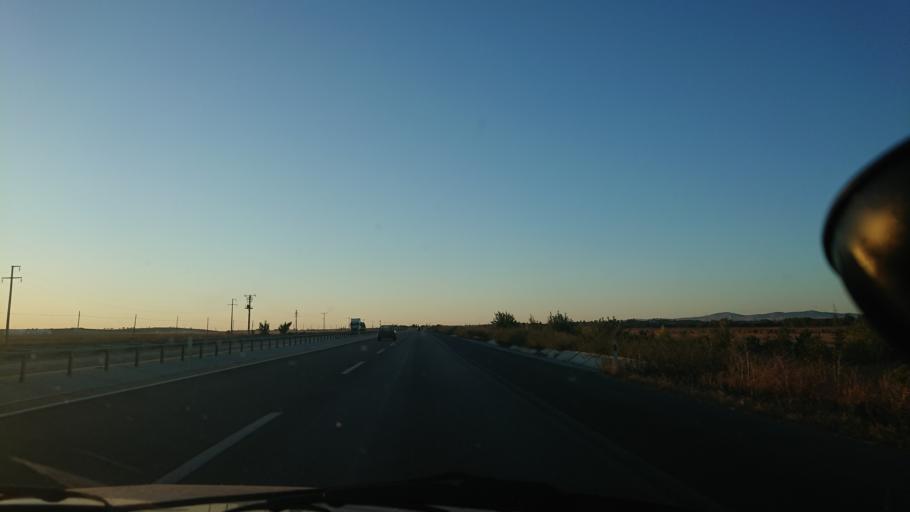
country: TR
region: Eskisehir
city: Mahmudiye
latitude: 39.5498
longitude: 30.9282
